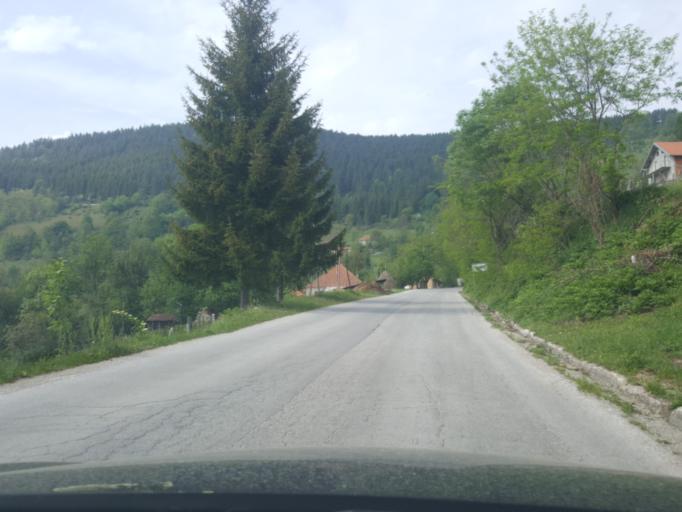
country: RS
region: Central Serbia
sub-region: Zlatiborski Okrug
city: Bajina Basta
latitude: 44.0766
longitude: 19.6624
